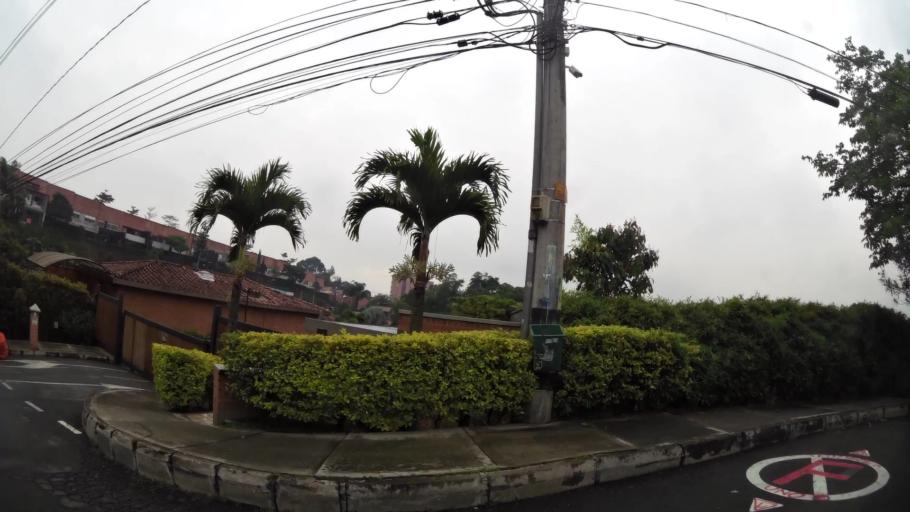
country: CO
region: Antioquia
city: Envigado
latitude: 6.1704
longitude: -75.5641
